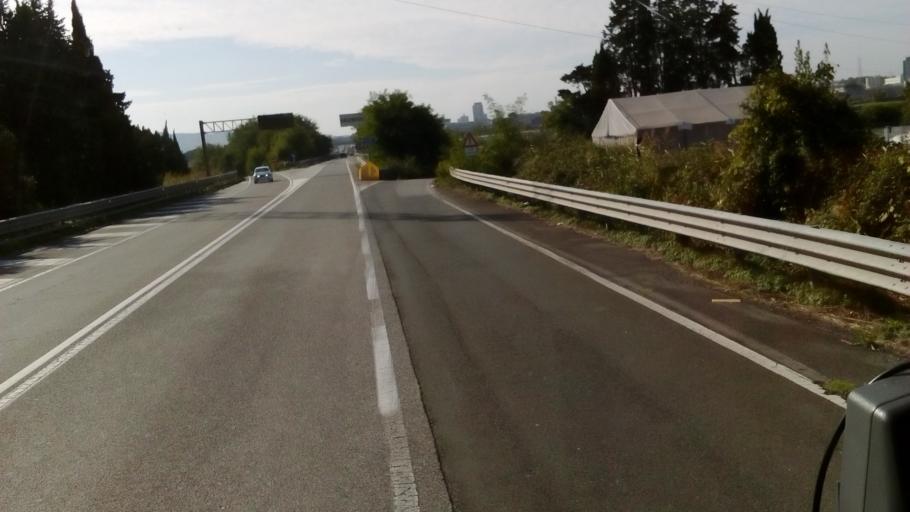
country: IT
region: Tuscany
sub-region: Provincia di Livorno
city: Livorno
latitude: 43.5809
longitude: 10.3493
